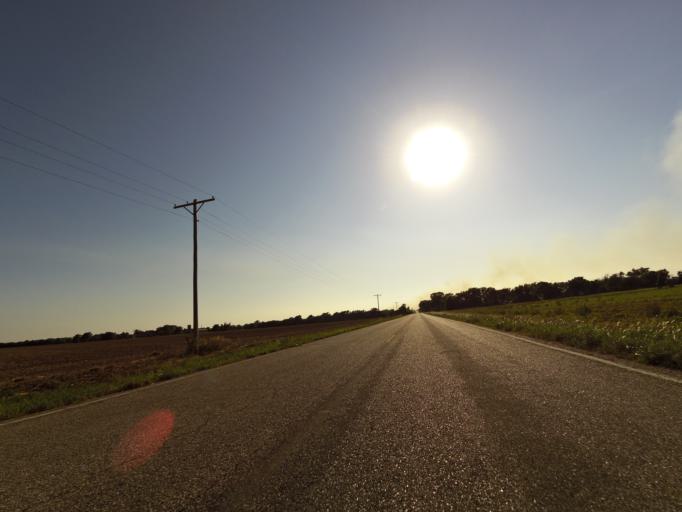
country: US
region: Kansas
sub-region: McPherson County
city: Moundridge
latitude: 38.1451
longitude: -97.5296
